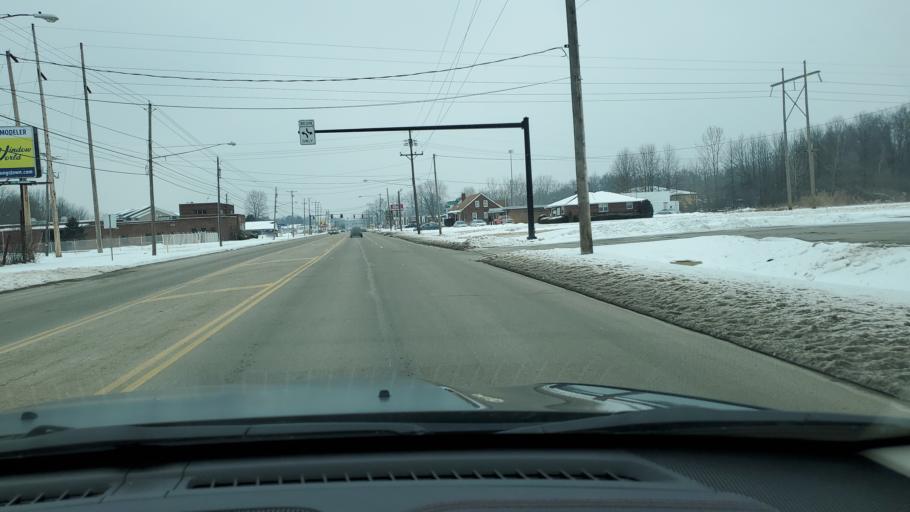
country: US
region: Ohio
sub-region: Trumbull County
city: Leavittsburg
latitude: 41.2491
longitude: -80.8504
